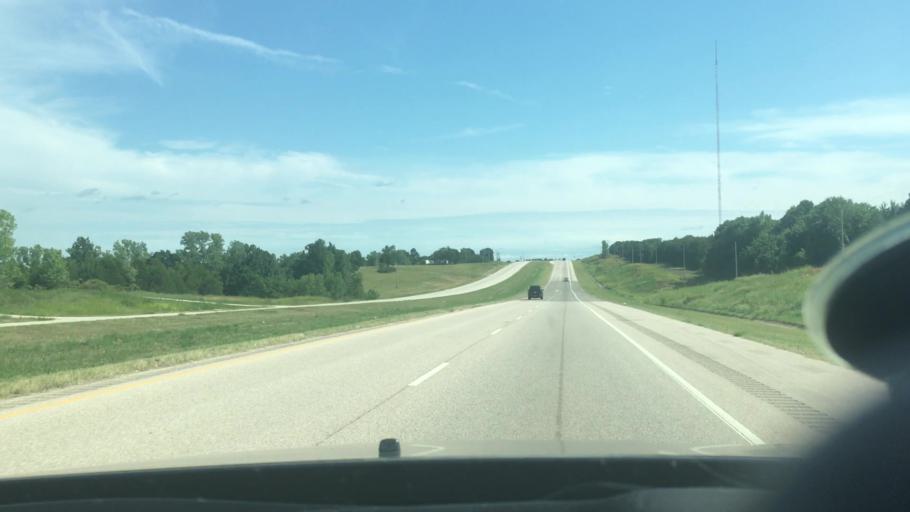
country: US
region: Oklahoma
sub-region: Pontotoc County
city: Byng
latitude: 34.9109
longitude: -96.6791
